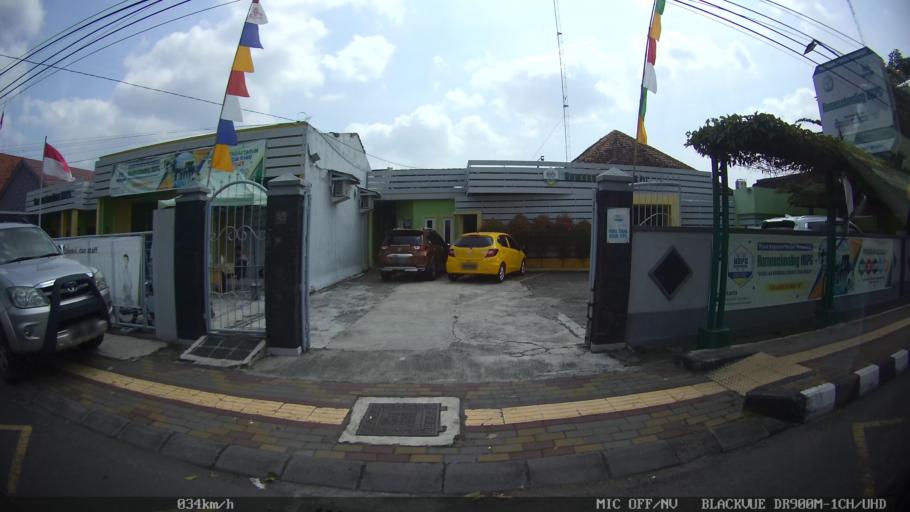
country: ID
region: Daerah Istimewa Yogyakarta
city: Yogyakarta
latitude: -7.7862
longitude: 110.3862
